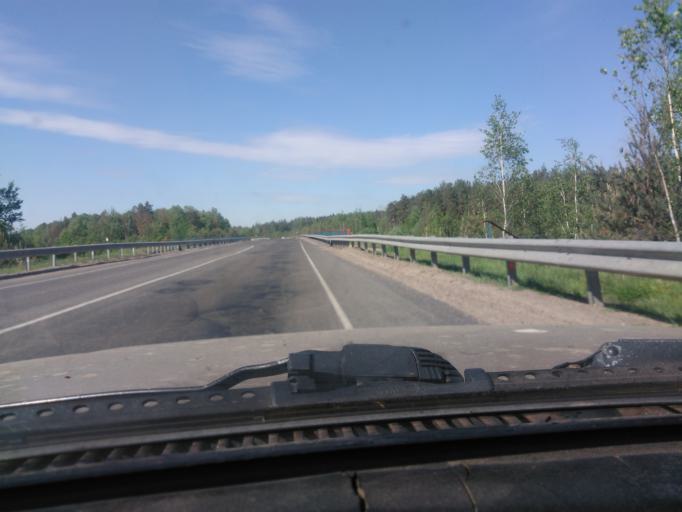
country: BY
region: Mogilev
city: Myazhysyatki
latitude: 53.8086
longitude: 30.2163
